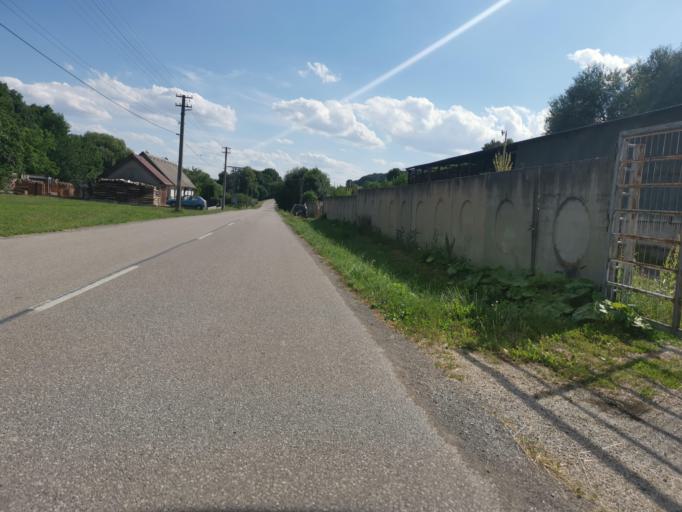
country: CZ
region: South Moravian
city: Knezdub
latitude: 48.7969
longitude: 17.4090
